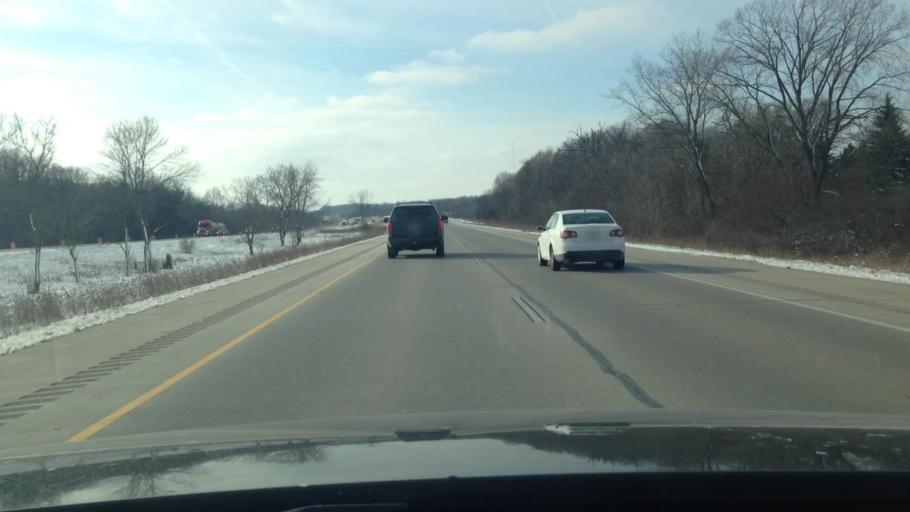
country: US
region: Wisconsin
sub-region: Waukesha County
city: Muskego
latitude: 42.9397
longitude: -88.1355
